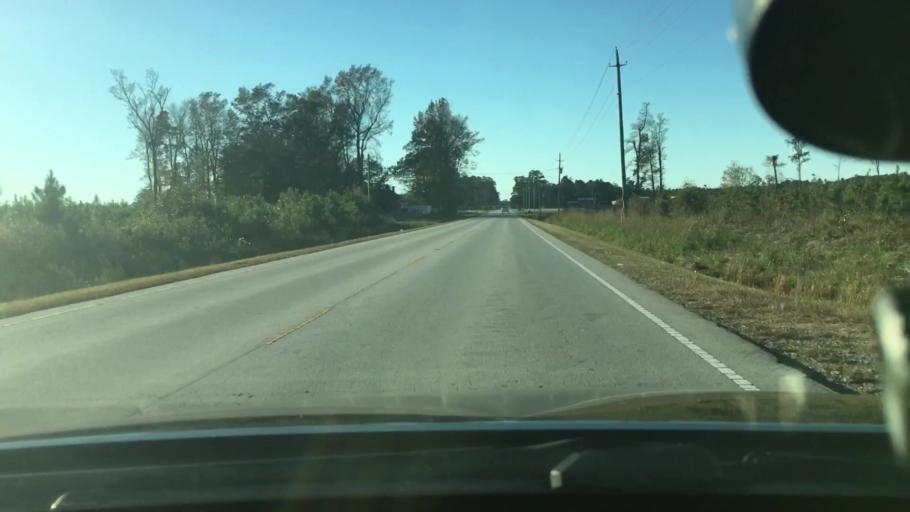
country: US
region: North Carolina
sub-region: Pitt County
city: Windsor
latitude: 35.4724
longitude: -77.2881
